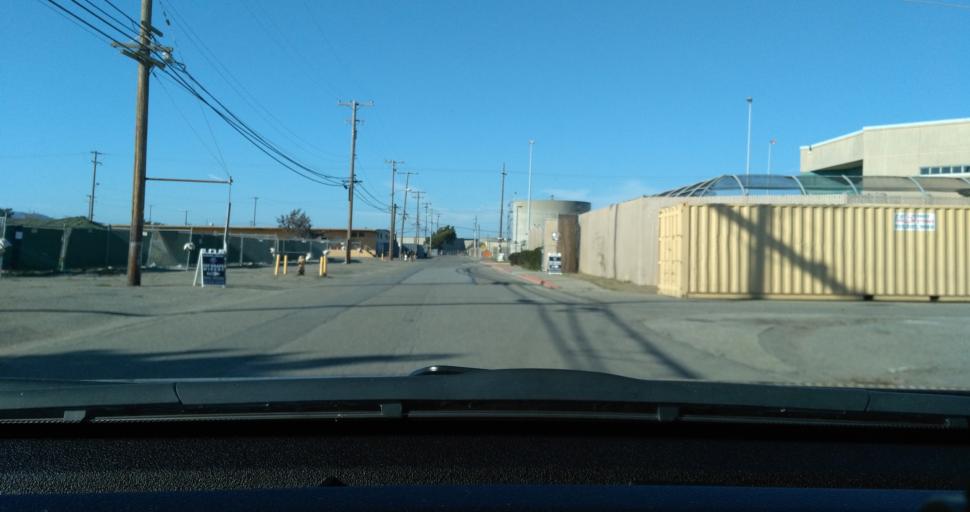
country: US
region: California
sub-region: San Francisco County
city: San Francisco
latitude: 37.8284
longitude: -122.3691
